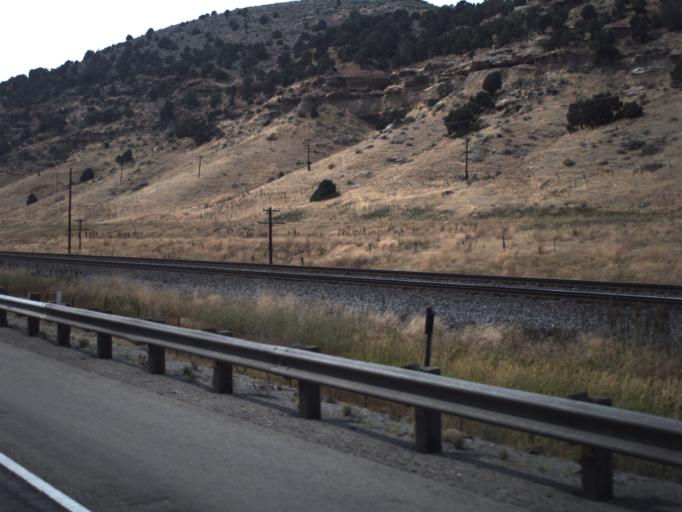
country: US
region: Utah
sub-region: Summit County
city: Coalville
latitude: 41.0422
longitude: -111.3210
